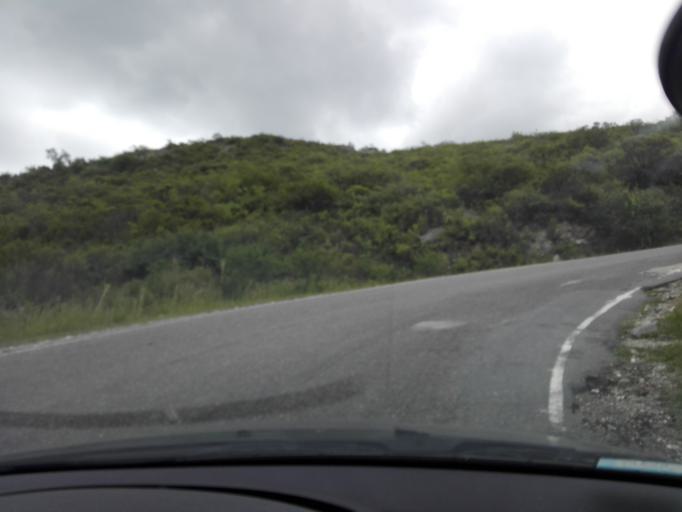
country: AR
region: Cordoba
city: Alta Gracia
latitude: -31.5915
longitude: -64.5022
